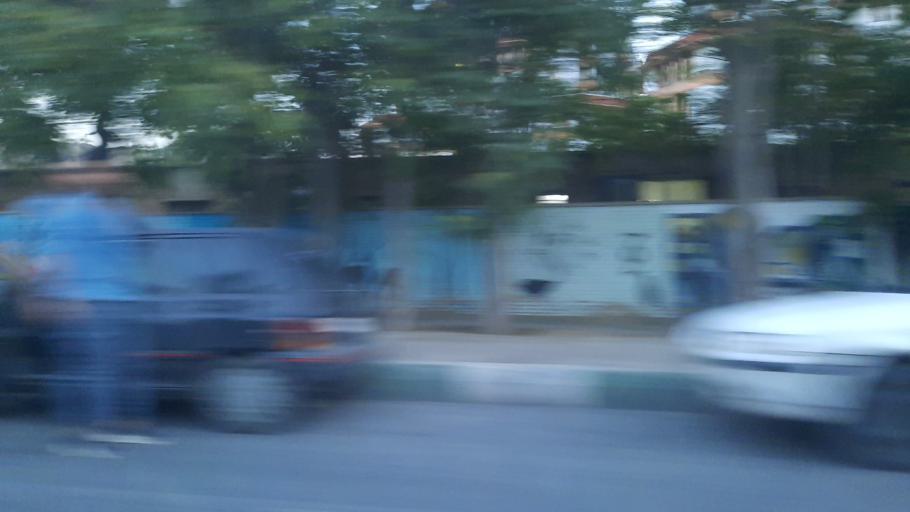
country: IR
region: Markazi
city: Arak
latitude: 34.0749
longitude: 49.7013
